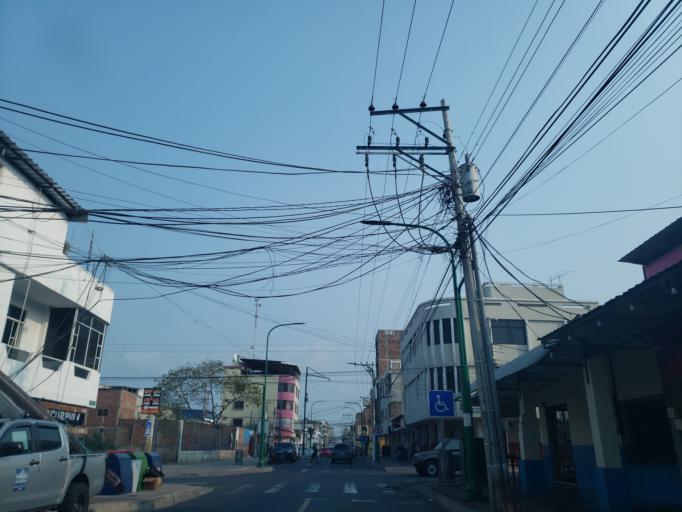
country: EC
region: Manabi
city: Manta
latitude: -0.9488
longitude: -80.7319
